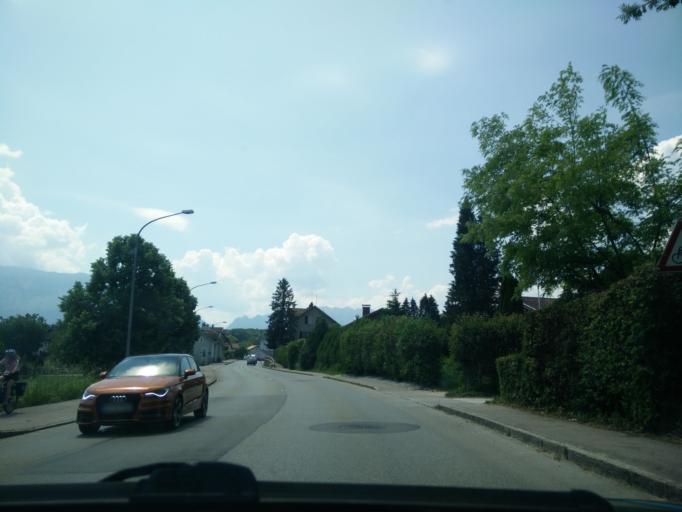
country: DE
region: Bavaria
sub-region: Upper Bavaria
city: Ainring
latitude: 47.7981
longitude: 12.9489
